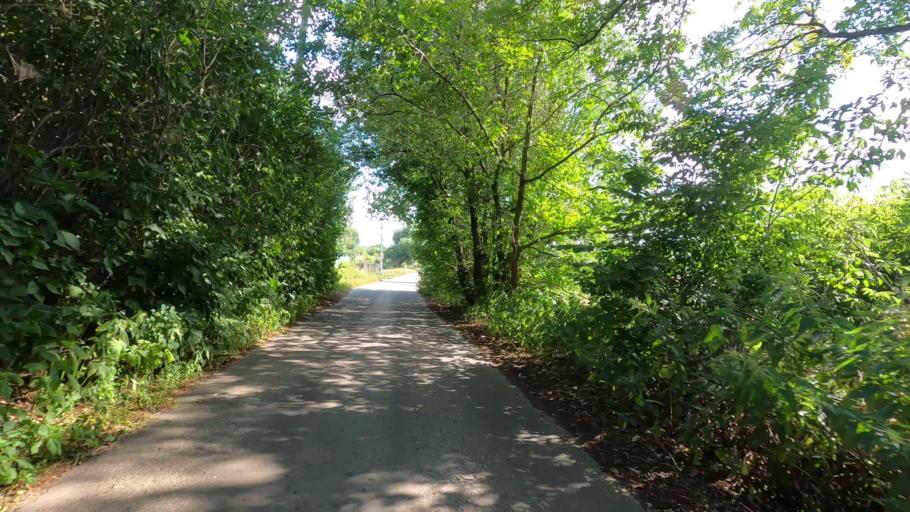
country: RU
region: Moskovskaya
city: Peski
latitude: 55.2111
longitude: 38.7497
